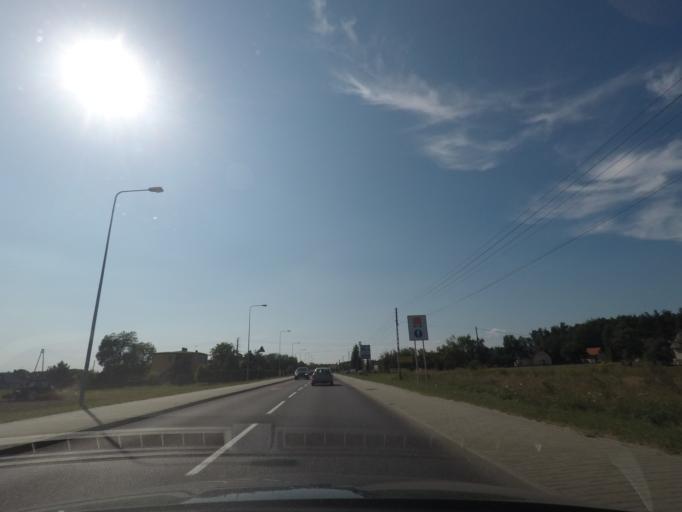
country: PL
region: Silesian Voivodeship
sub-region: Powiat pszczynski
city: Rudziczka
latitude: 50.0374
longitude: 18.7504
